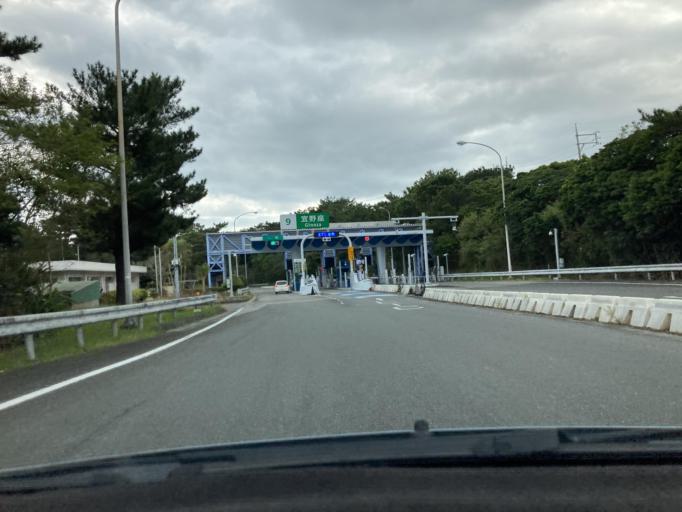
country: JP
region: Okinawa
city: Nago
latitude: 26.4878
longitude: 127.9699
